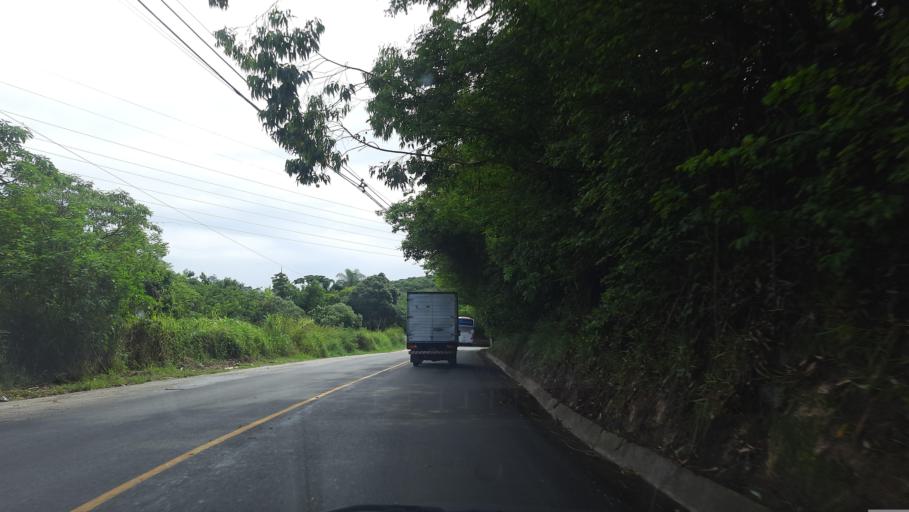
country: BR
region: Sao Paulo
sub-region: Caieiras
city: Caieiras
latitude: -23.3657
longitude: -46.6731
